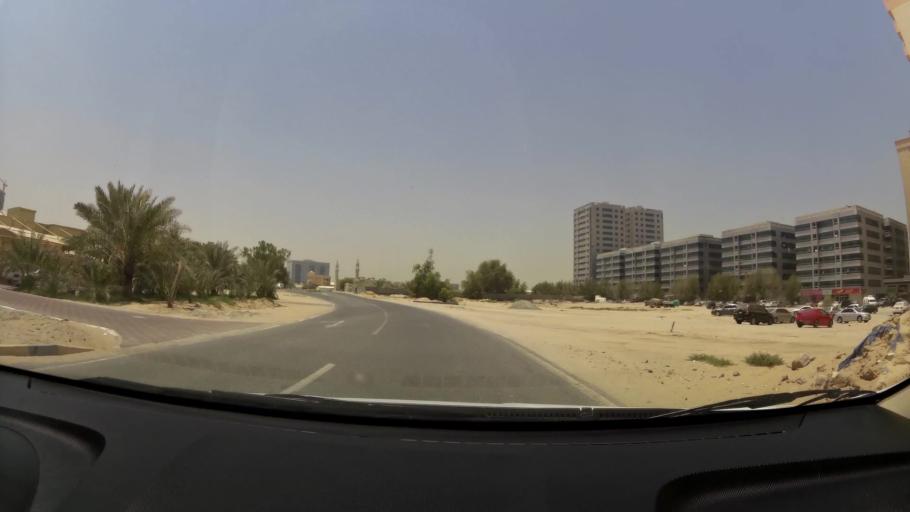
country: AE
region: Ajman
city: Ajman
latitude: 25.4040
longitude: 55.5090
